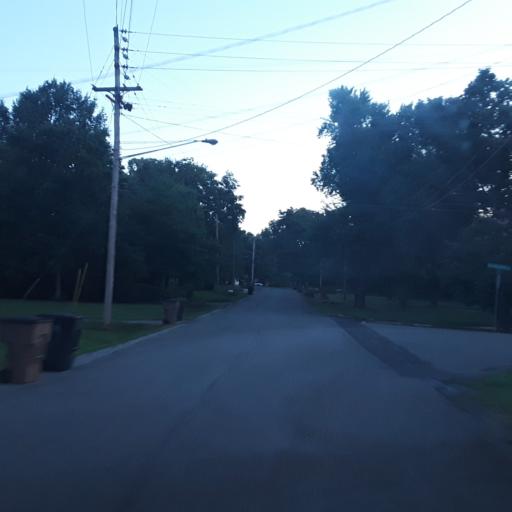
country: US
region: Tennessee
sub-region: Davidson County
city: Oak Hill
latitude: 36.0736
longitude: -86.7623
